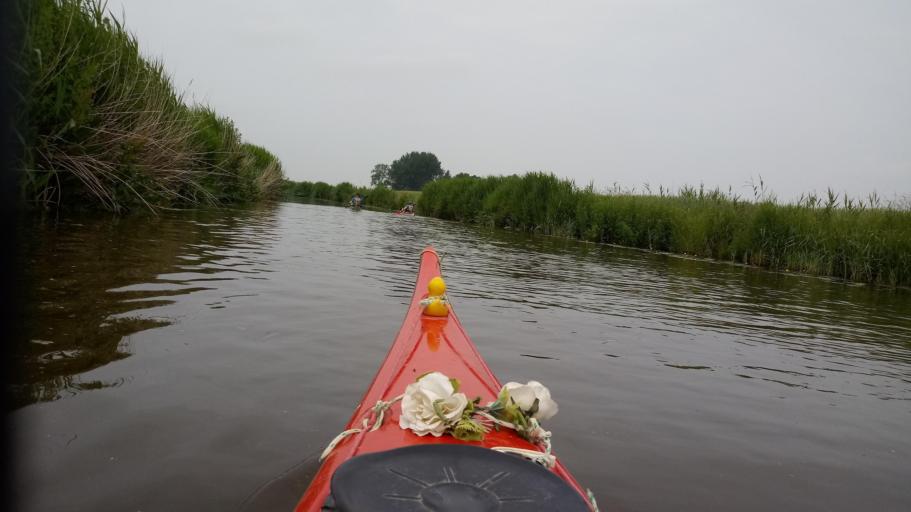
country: NL
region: Groningen
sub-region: Gemeente Winsum
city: Winsum
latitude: 53.3626
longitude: 6.5348
